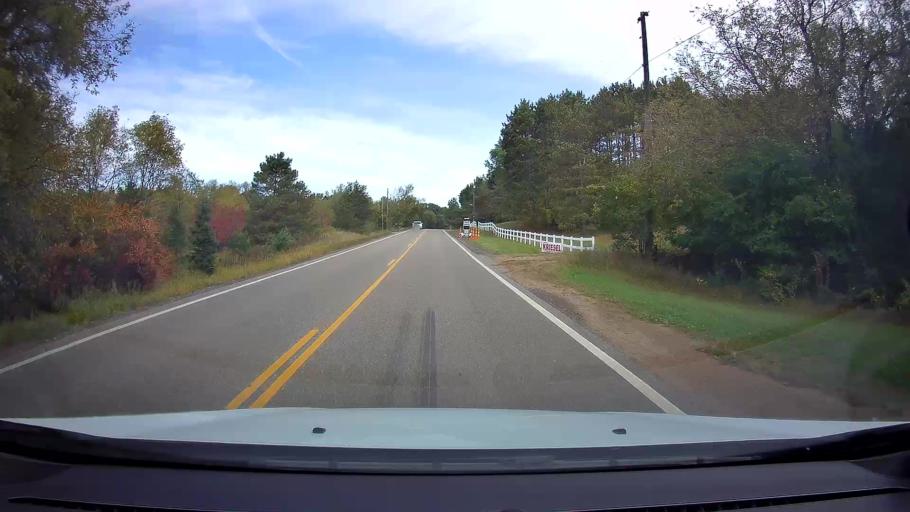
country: US
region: Minnesota
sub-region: Washington County
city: Stillwater
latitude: 45.0863
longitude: -92.8247
